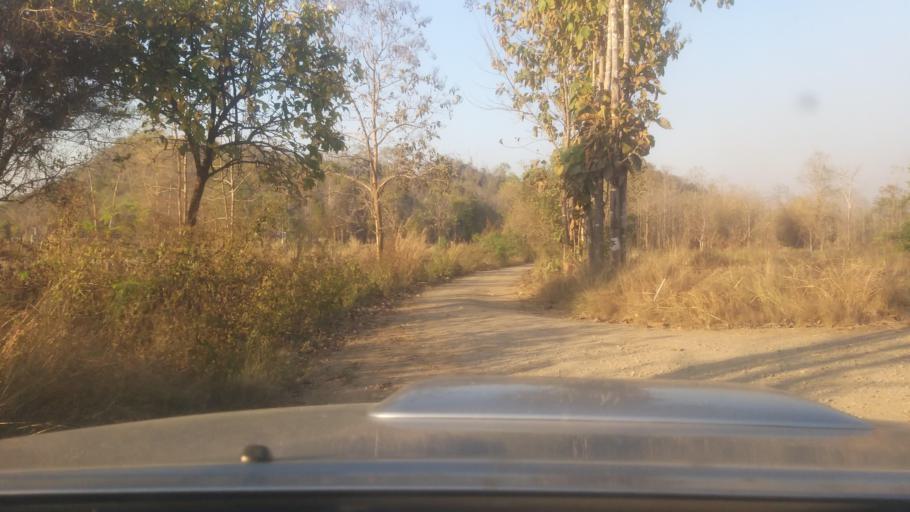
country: TH
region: Phrae
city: Nong Muang Khai
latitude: 18.2937
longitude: 100.0371
